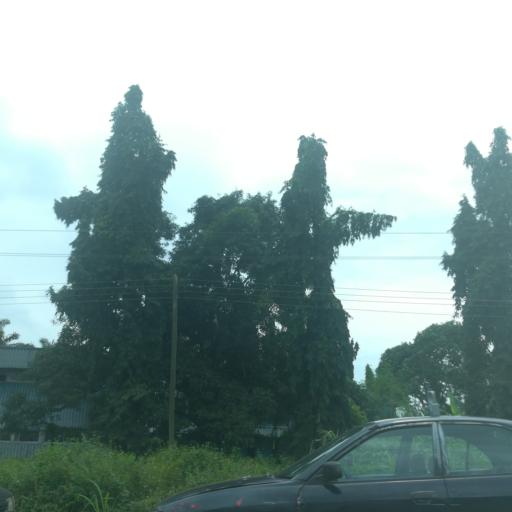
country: NG
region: Lagos
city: Ejirin
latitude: 6.6512
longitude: 3.7129
